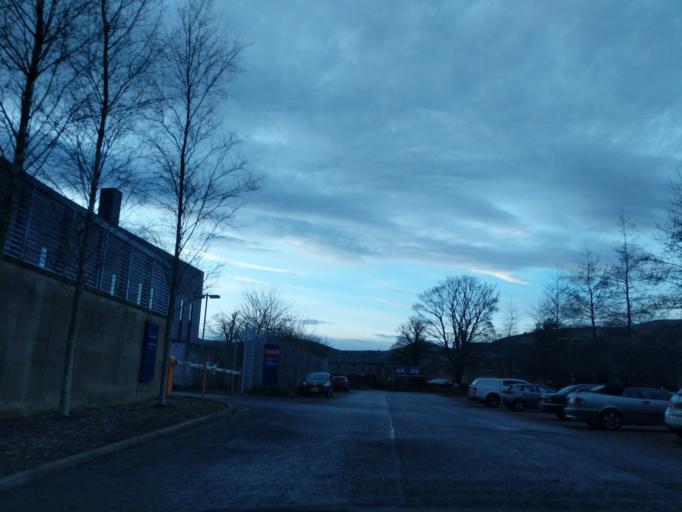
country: GB
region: Scotland
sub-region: Midlothian
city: Loanhead
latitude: 55.8658
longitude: -3.1974
